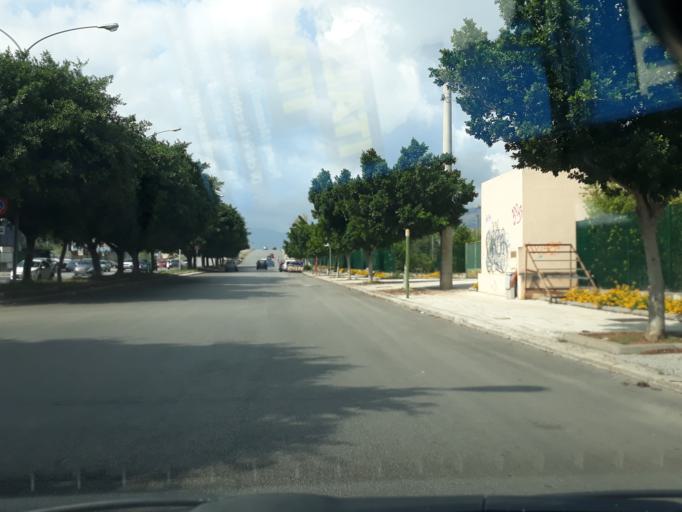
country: IT
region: Sicily
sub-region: Palermo
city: Palermo
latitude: 38.0960
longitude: 13.3429
